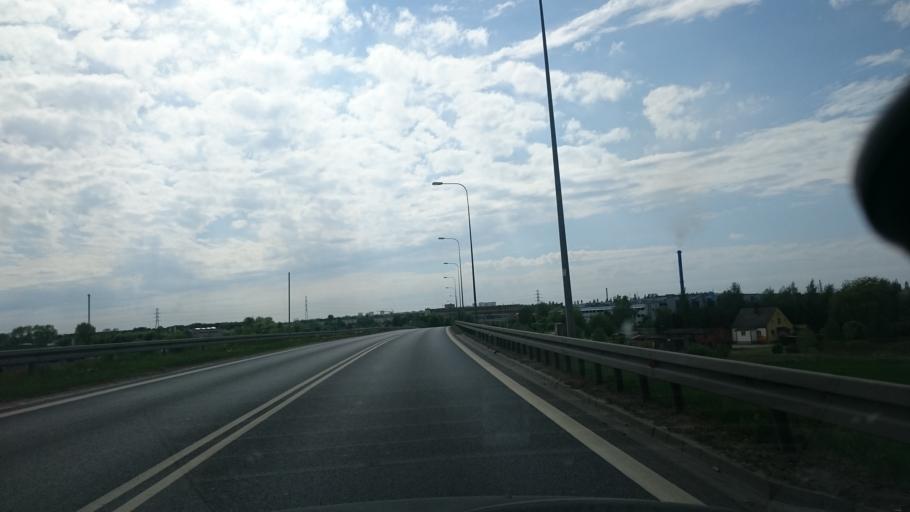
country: PL
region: Kujawsko-Pomorskie
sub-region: Grudziadz
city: Grudziadz
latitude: 53.4799
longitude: 18.7864
